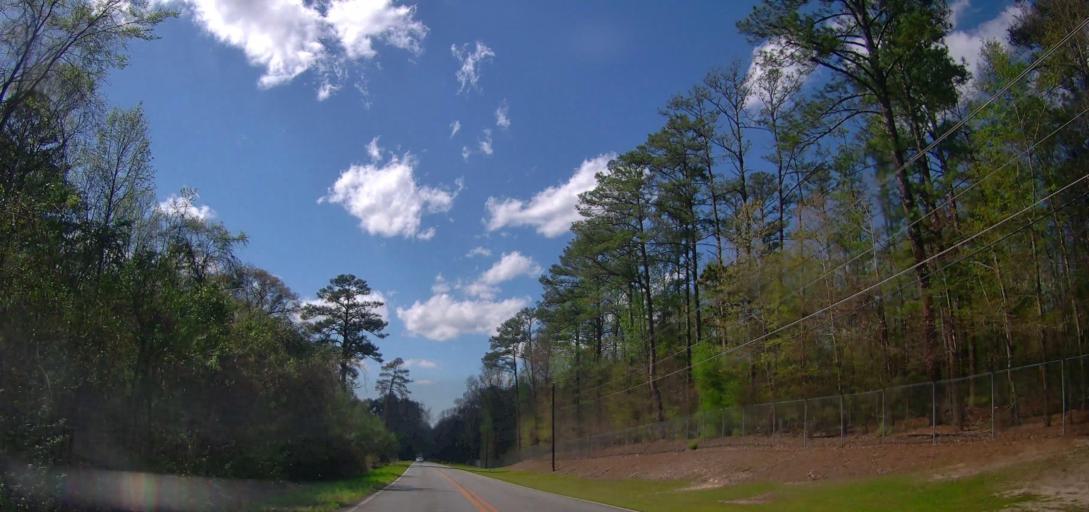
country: US
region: Georgia
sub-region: Bibb County
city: Macon
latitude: 32.8146
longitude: -83.5423
